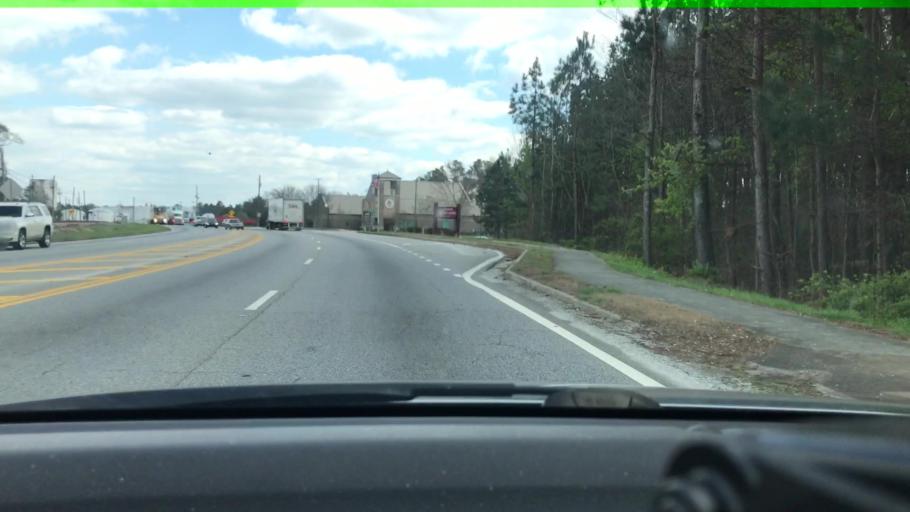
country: US
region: Georgia
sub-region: Clarke County
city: Country Club Estates
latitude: 33.9897
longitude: -83.4290
